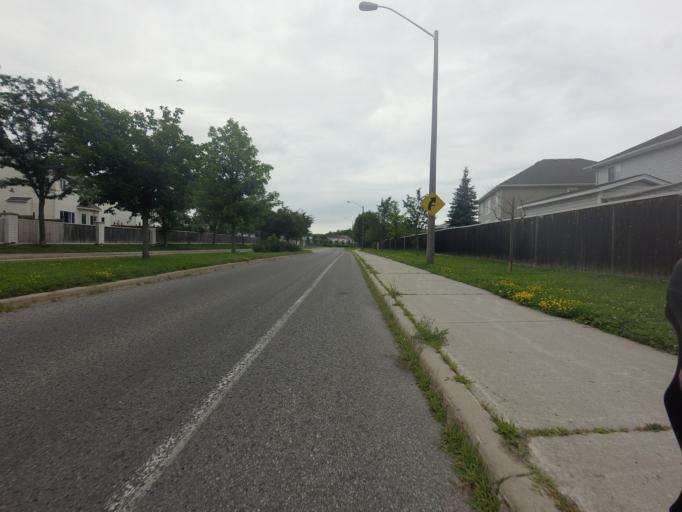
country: CA
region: Ontario
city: Ottawa
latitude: 45.2889
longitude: -75.7101
